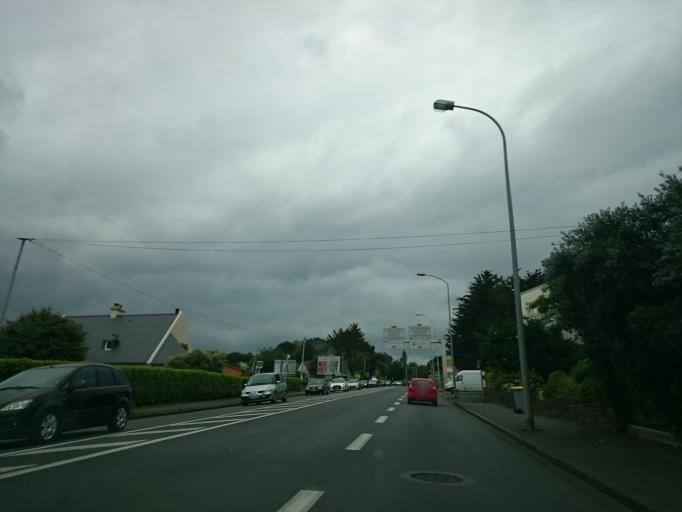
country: FR
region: Brittany
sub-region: Departement des Cotes-d'Armor
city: Lannion
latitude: 48.7364
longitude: -3.4682
